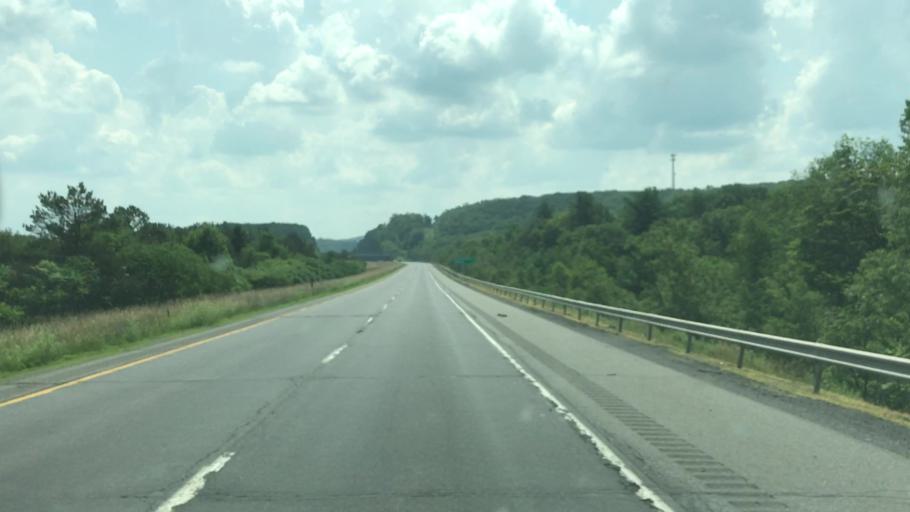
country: US
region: Pennsylvania
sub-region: Lackawanna County
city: Mount Cobb
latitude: 41.4008
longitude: -75.4899
